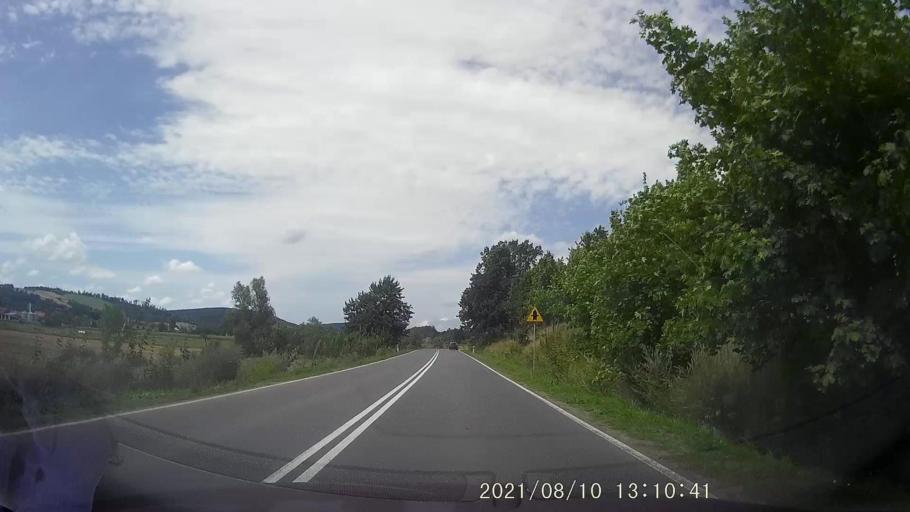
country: PL
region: Lower Silesian Voivodeship
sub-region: Powiat klodzki
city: Bozkow
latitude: 50.5039
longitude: 16.5256
